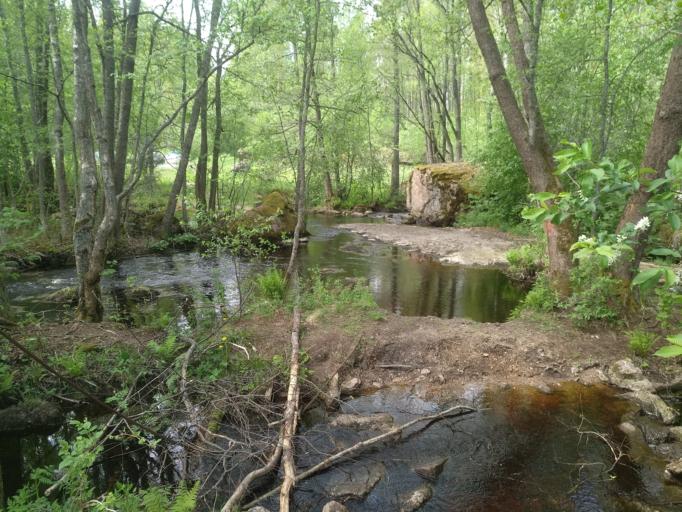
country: RU
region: Leningrad
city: Veshchevo
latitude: 60.7793
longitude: 29.0969
